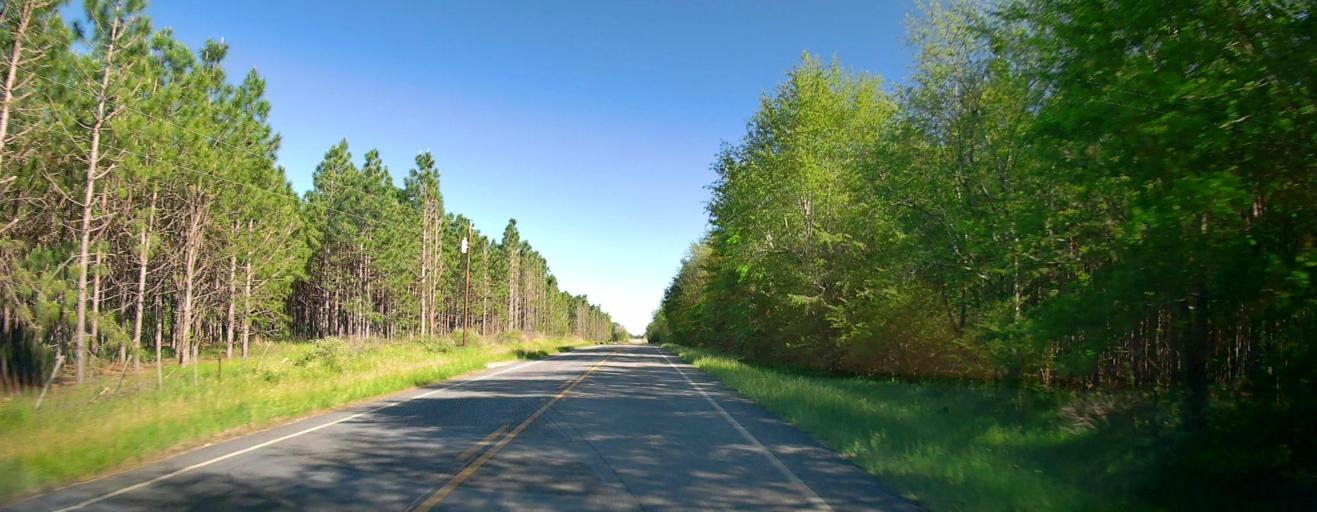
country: US
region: Georgia
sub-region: Wilcox County
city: Rochelle
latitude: 31.9973
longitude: -83.4755
